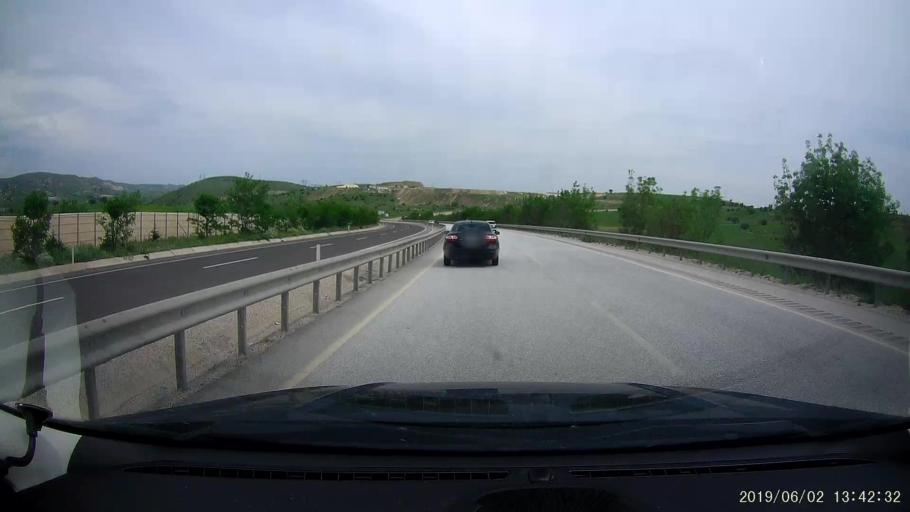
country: TR
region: Cankiri
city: Kursunlu
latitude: 40.8403
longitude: 33.1994
